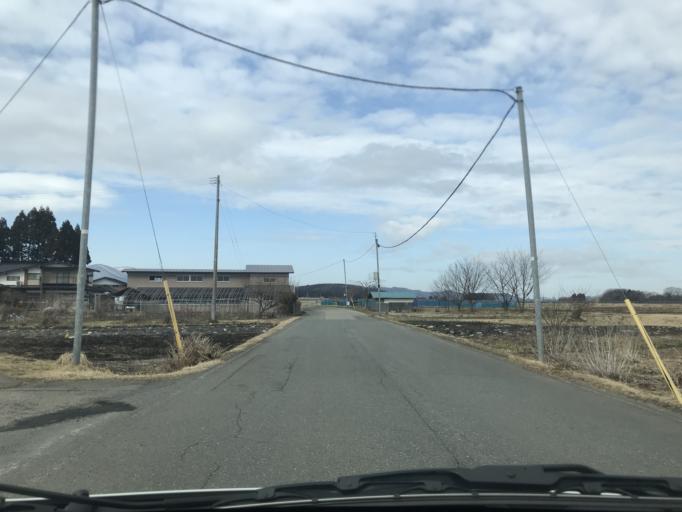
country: JP
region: Iwate
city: Hanamaki
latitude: 39.3386
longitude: 140.9831
